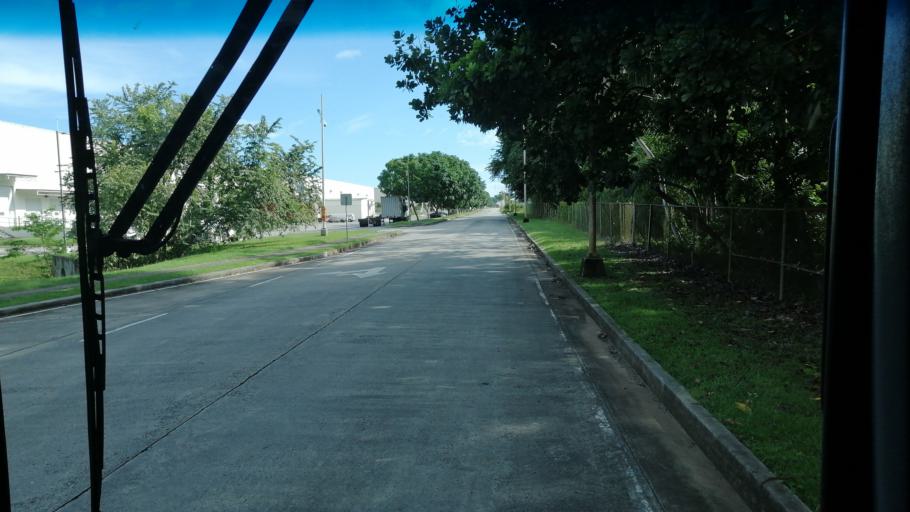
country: PA
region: Panama
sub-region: Distrito de Panama
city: Ancon
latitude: 8.9251
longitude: -79.5944
